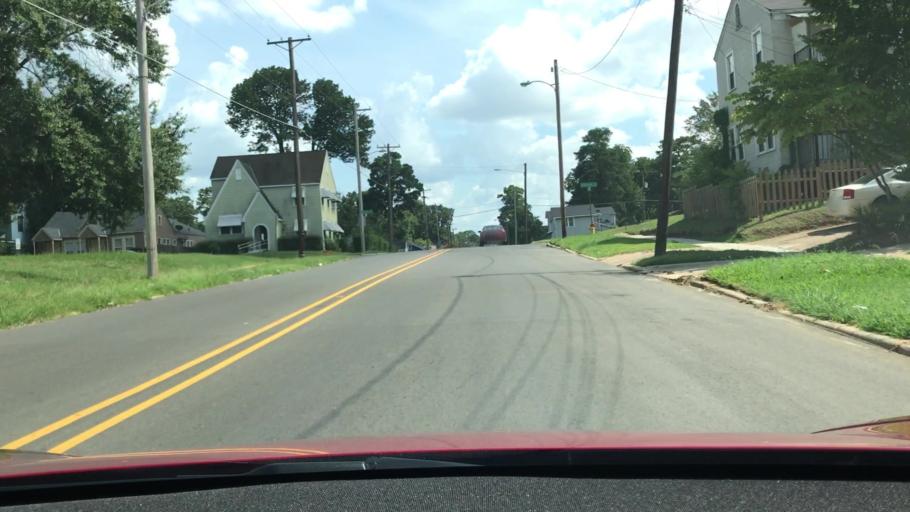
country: US
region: Louisiana
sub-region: Bossier Parish
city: Bossier City
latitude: 32.4901
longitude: -93.7332
